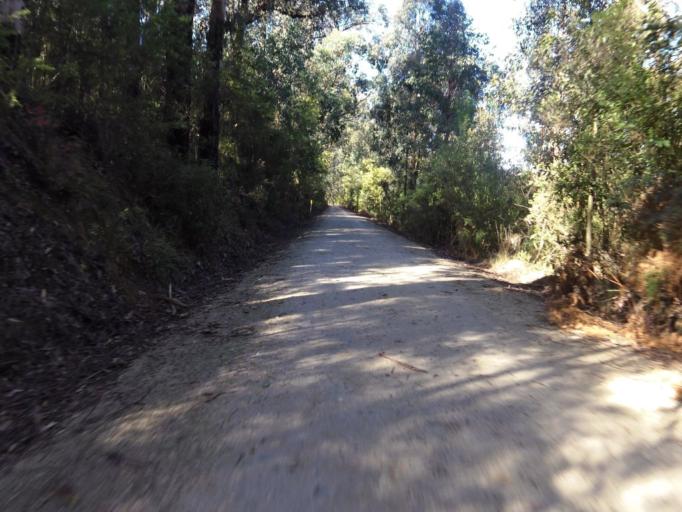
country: AU
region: Victoria
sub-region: Latrobe
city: Moe
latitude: -38.3899
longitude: 146.1840
